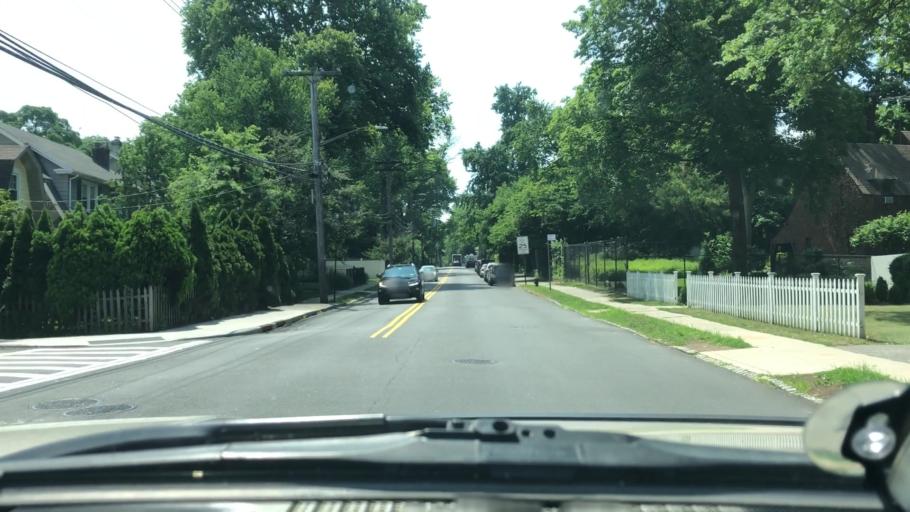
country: US
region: New Jersey
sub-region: Hudson County
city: Bayonne
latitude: 40.6269
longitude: -74.1153
